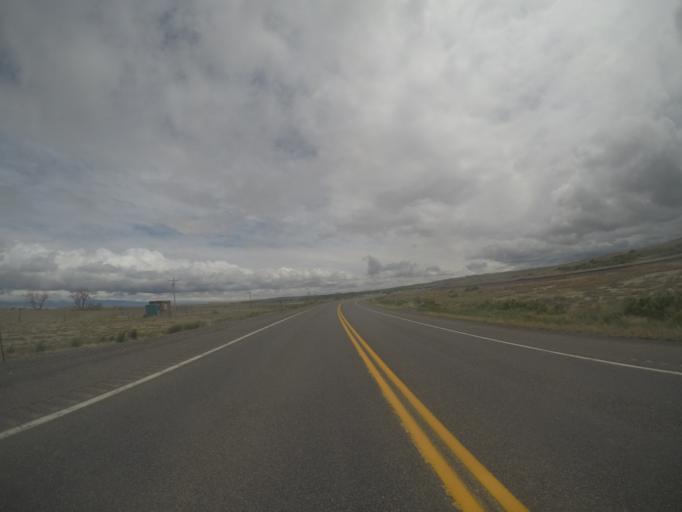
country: US
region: Wyoming
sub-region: Park County
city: Powell
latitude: 44.9090
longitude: -108.6033
